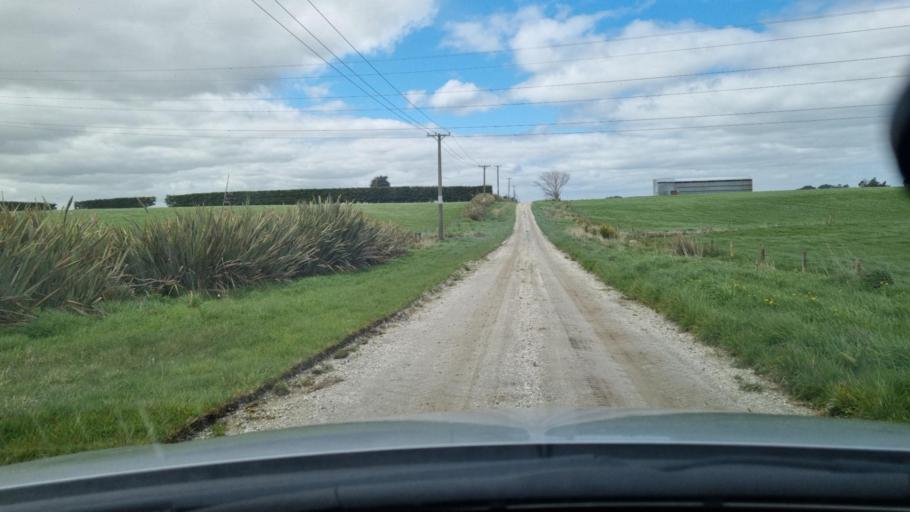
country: NZ
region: Southland
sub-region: Invercargill City
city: Invercargill
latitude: -46.4429
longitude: 168.4510
